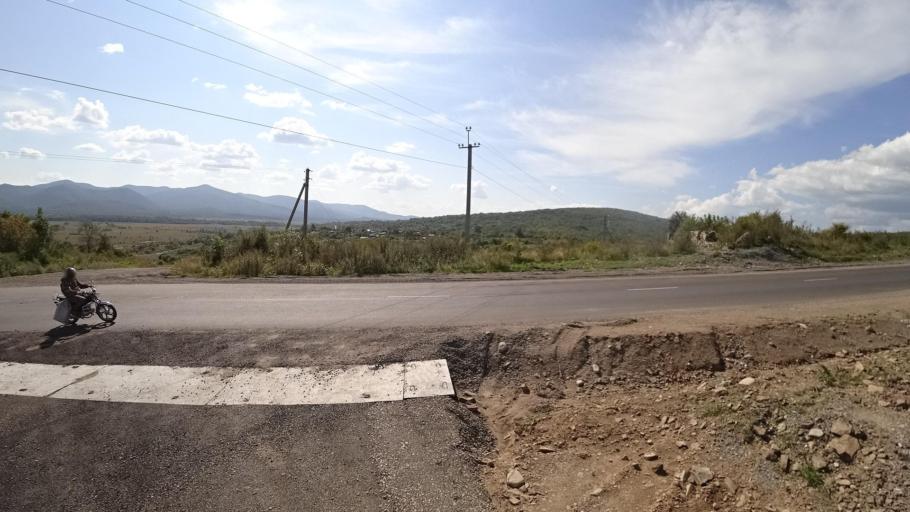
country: RU
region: Jewish Autonomous Oblast
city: Londoko
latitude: 49.0075
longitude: 131.8659
